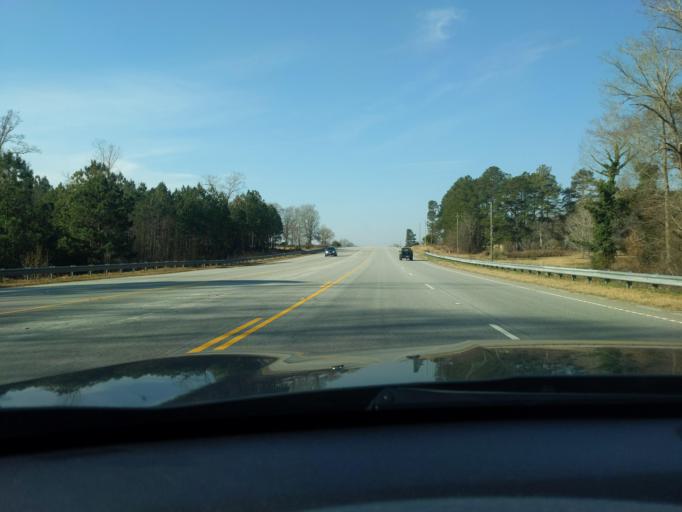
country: US
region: South Carolina
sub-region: Abbeville County
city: Abbeville
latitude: 34.1290
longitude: -82.4297
